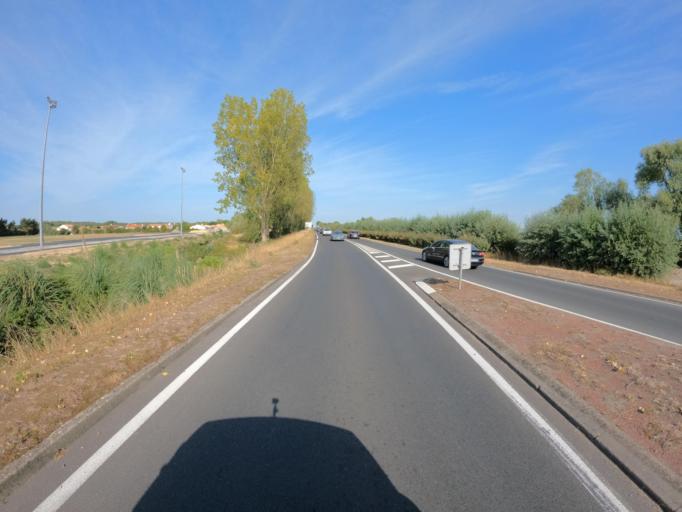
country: FR
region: Pays de la Loire
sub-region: Departement de la Vendee
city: Saint-Jean-de-Monts
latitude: 46.7985
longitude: -2.0557
